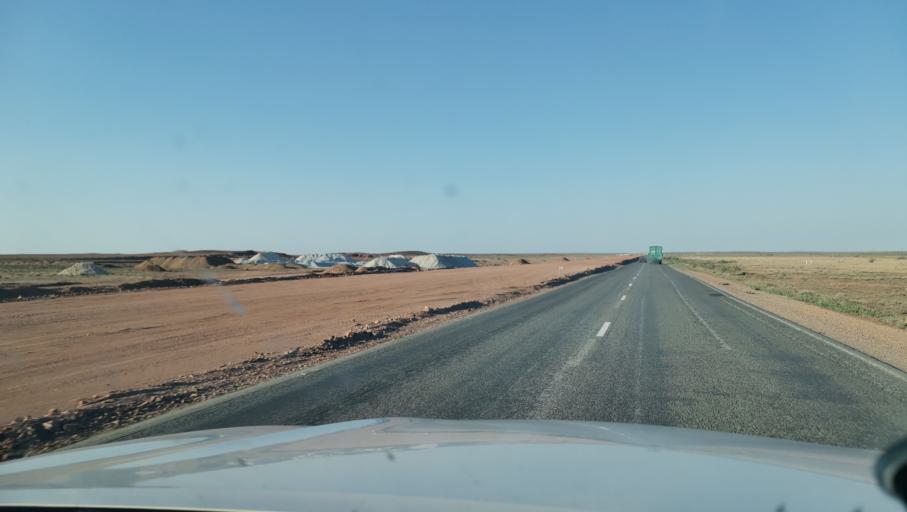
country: KZ
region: Qaraghandy
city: Saryshaghan
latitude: 46.4644
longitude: 74.0208
